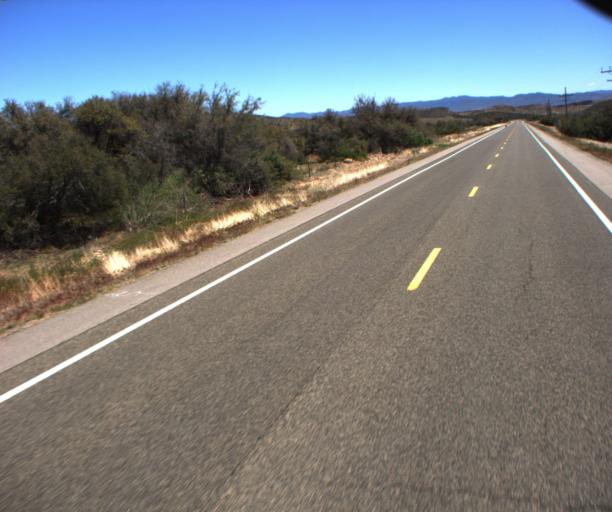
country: US
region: Arizona
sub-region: Yavapai County
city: Congress
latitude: 34.3053
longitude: -112.7162
